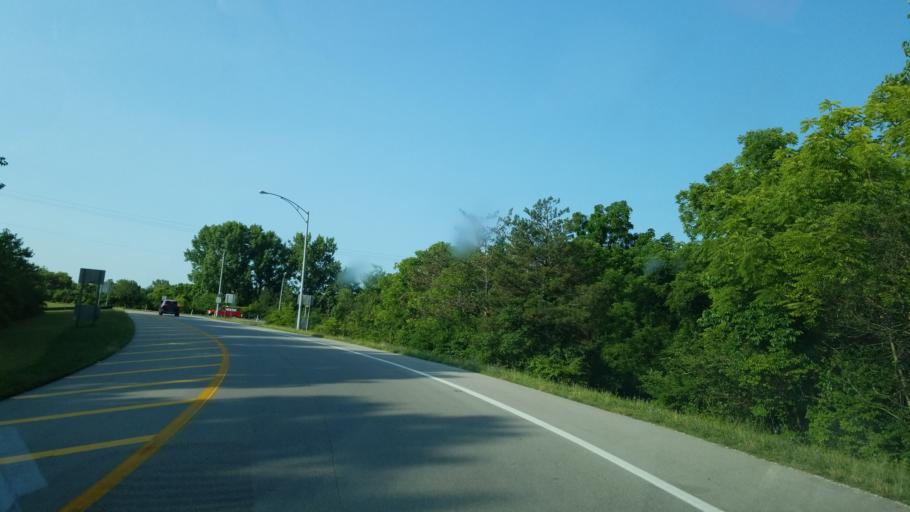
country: US
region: Ohio
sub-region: Franklin County
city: Worthington
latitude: 40.0642
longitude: -83.0344
